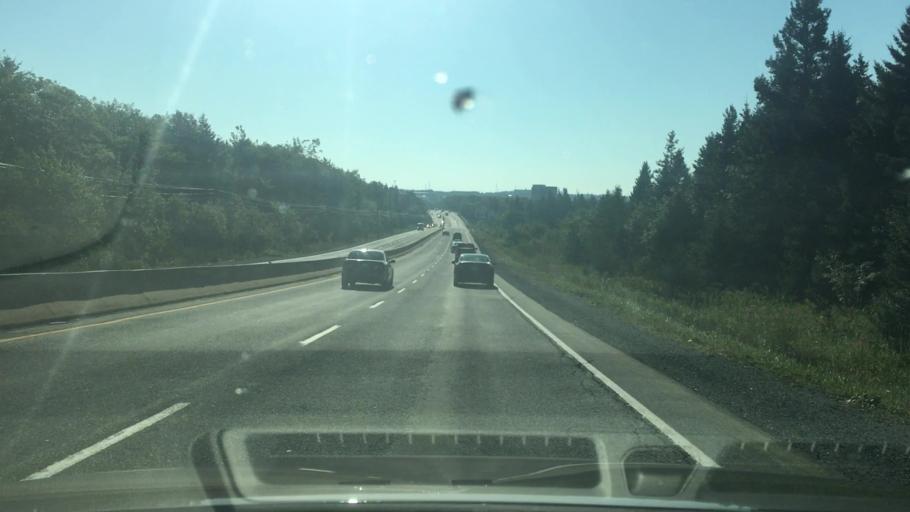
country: CA
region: Nova Scotia
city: Dartmouth
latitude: 44.7082
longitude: -63.6232
